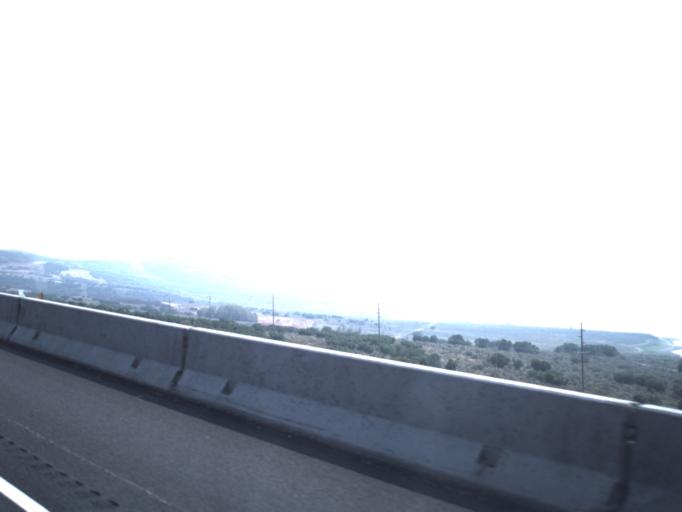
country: US
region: Utah
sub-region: Summit County
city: Park City
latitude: 40.6548
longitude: -111.4111
